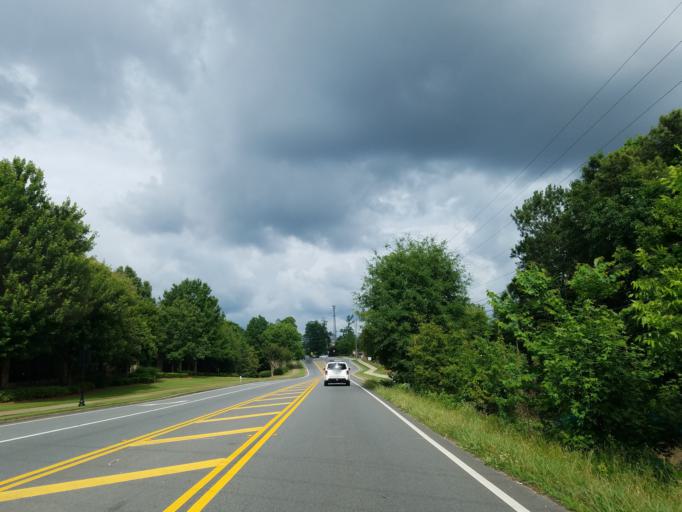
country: US
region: Georgia
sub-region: Fulton County
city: Milton
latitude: 34.1260
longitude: -84.2662
